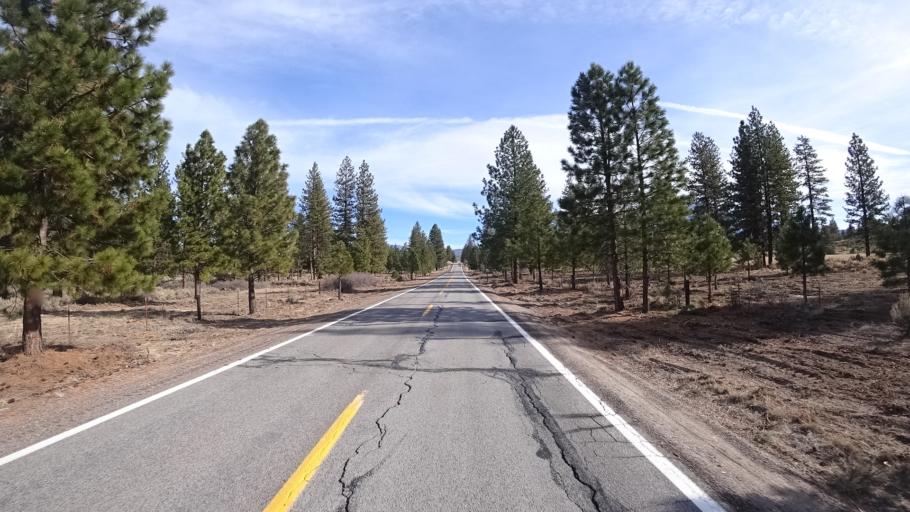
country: US
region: California
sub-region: Siskiyou County
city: Weed
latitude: 41.4940
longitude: -122.3832
